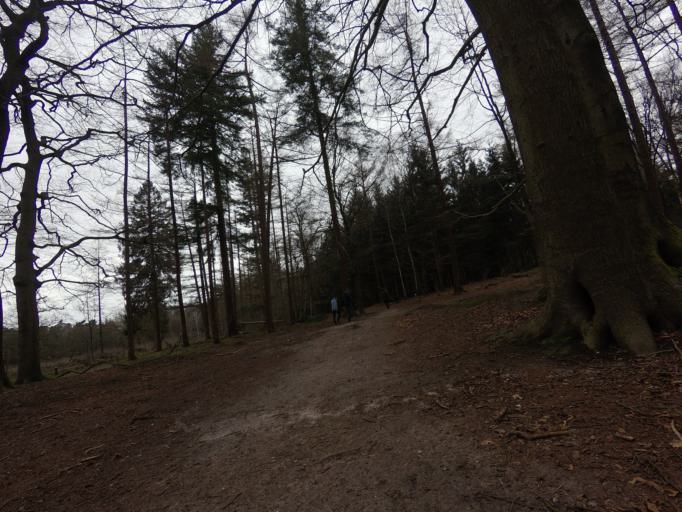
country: NL
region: Utrecht
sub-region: Gemeente Utrechtse Heuvelrug
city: Doorn
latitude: 52.0415
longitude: 5.3626
